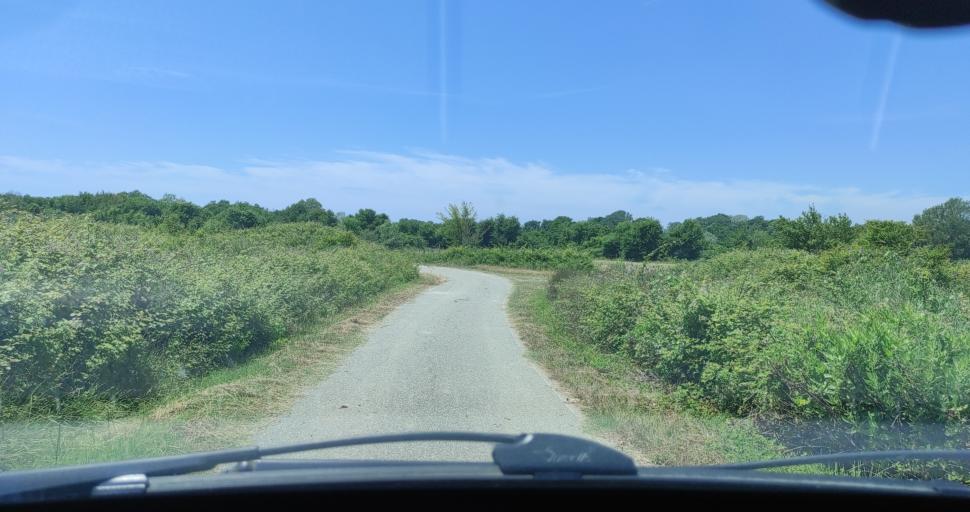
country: AL
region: Shkoder
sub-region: Rrethi i Shkodres
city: Velipoje
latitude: 41.8816
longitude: 19.3837
